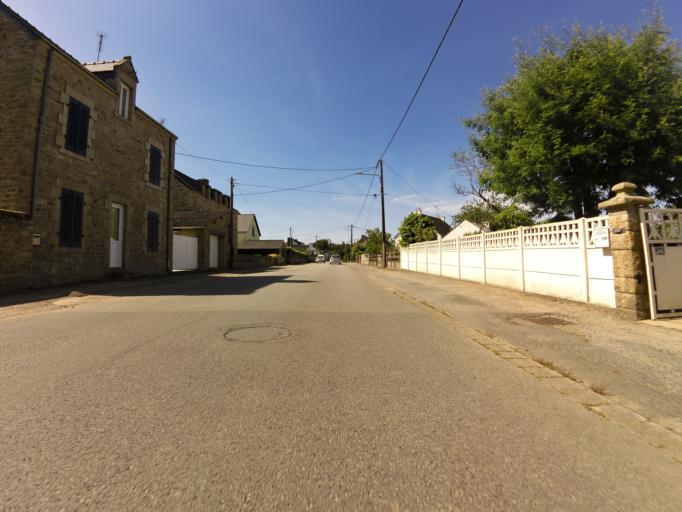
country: FR
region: Brittany
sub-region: Departement du Morbihan
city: Malansac
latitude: 47.6801
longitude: -2.2994
